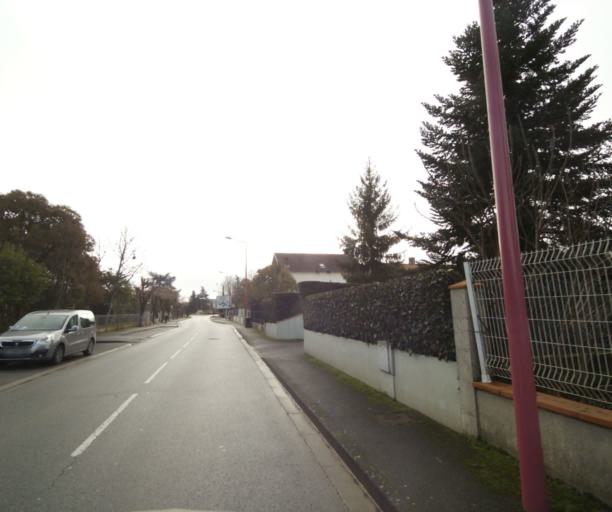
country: FR
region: Midi-Pyrenees
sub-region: Departement de la Haute-Garonne
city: Villemur-sur-Tarn
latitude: 43.8684
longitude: 1.4968
